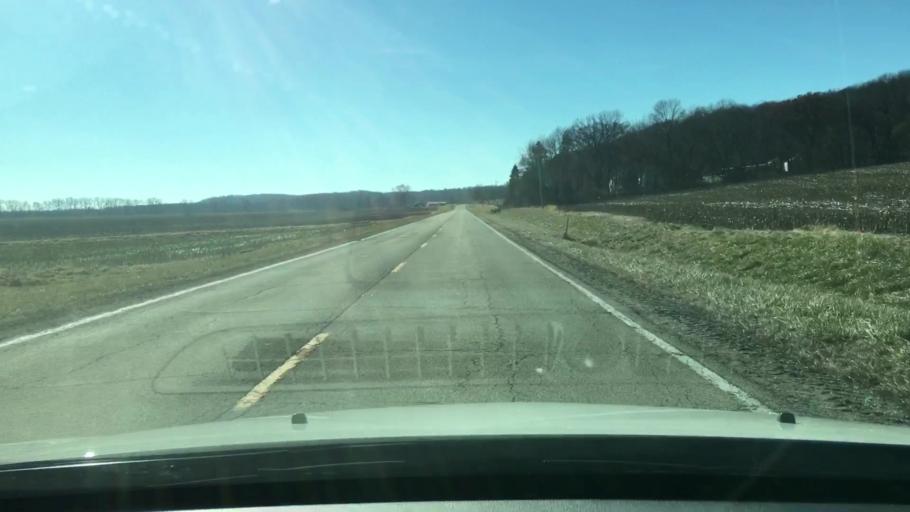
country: US
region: Illinois
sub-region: Mason County
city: Havana
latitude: 40.2404
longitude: -90.1921
